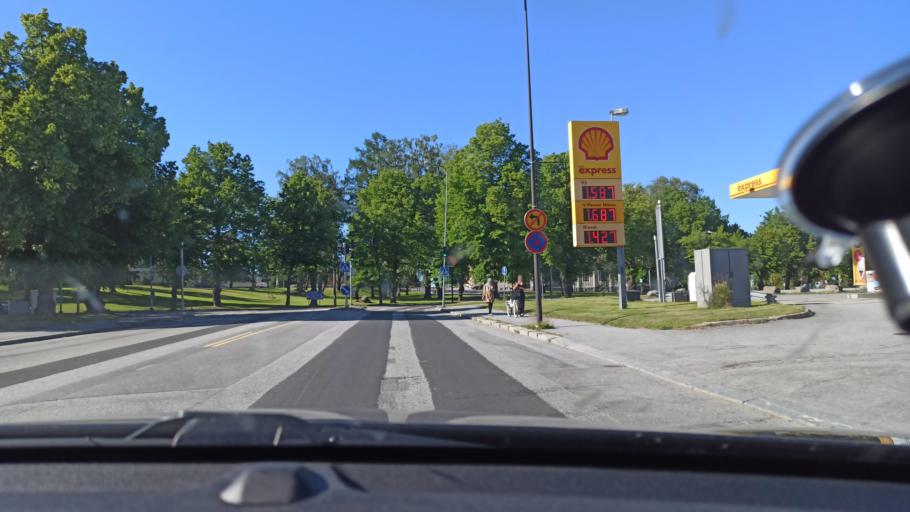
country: FI
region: Ostrobothnia
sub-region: Jakobstadsregionen
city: Jakobstad
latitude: 63.6764
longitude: 22.7111
